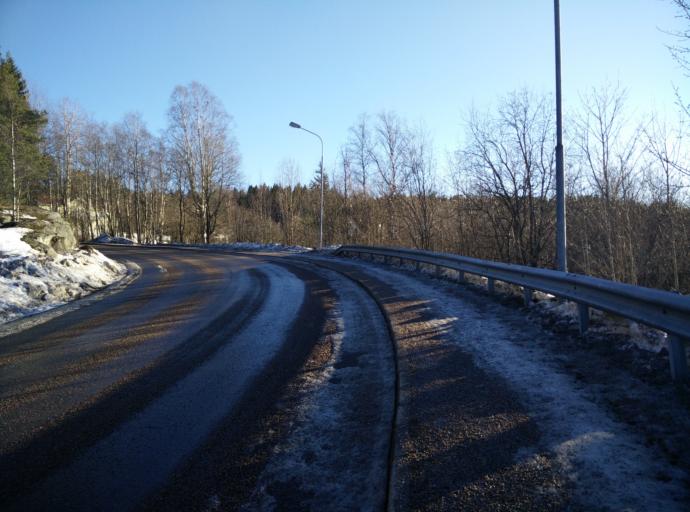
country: SE
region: Vaesternorrland
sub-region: Sundsvalls Kommun
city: Skottsund
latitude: 62.3079
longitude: 17.3895
